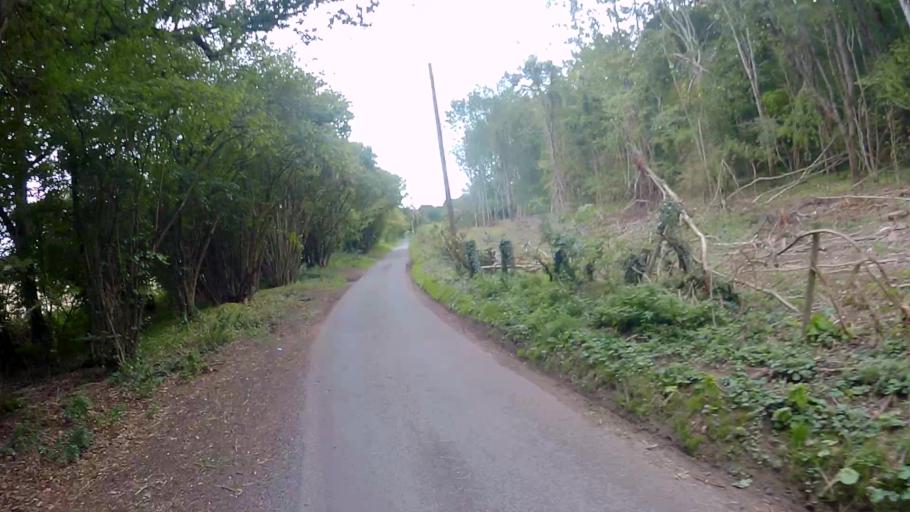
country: GB
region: England
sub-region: Hampshire
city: Overton
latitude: 51.2153
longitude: -1.2261
